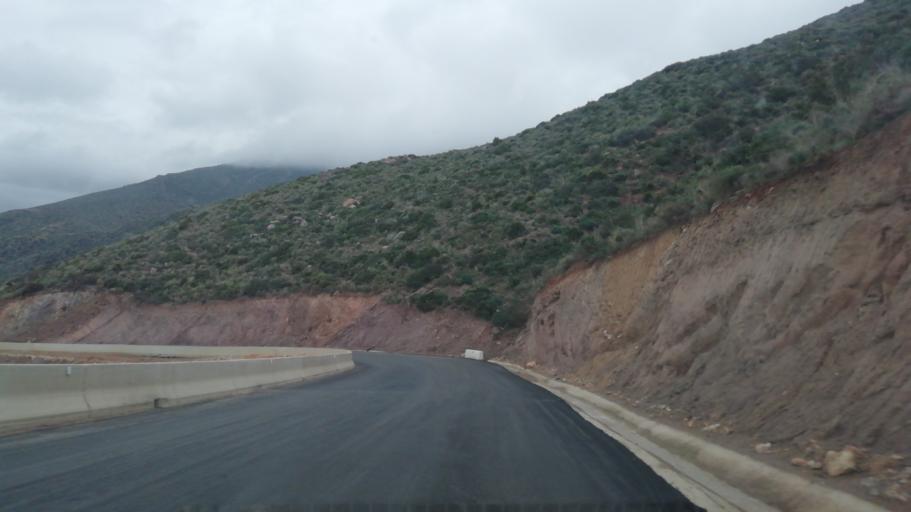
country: DZ
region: Oran
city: Bir el Djir
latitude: 35.7685
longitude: -0.5210
